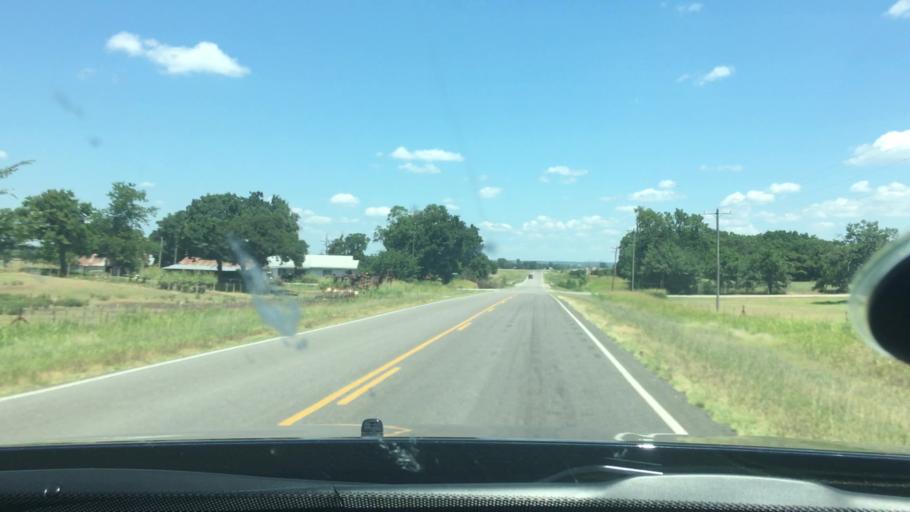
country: US
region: Oklahoma
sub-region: Carter County
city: Dickson
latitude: 34.2147
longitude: -96.9771
